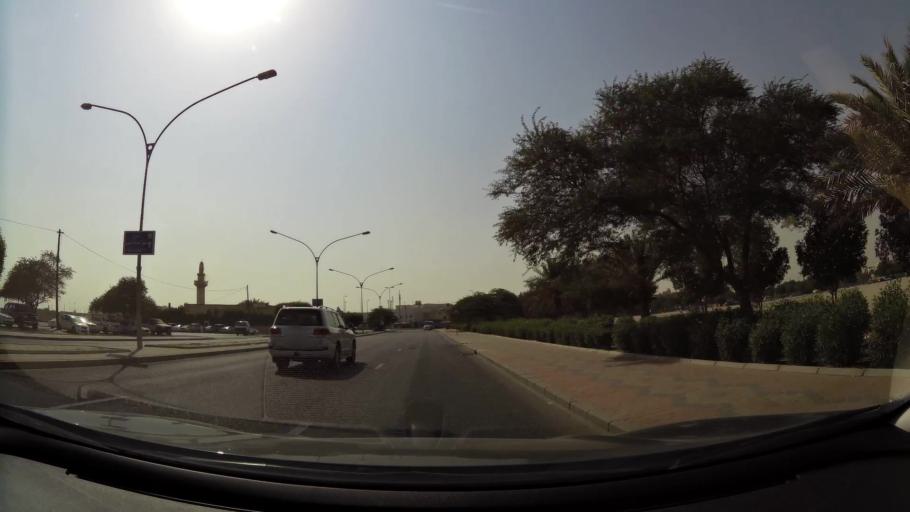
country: KW
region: Al Ahmadi
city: Al Fahahil
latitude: 29.0781
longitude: 48.1255
